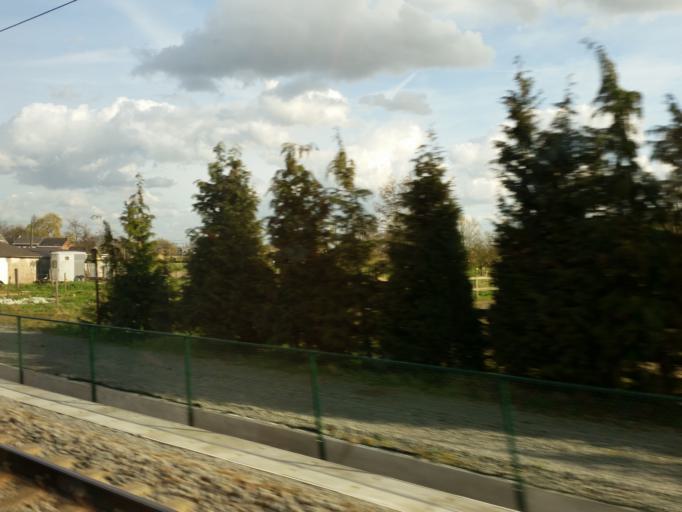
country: BE
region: Flanders
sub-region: Provincie Vlaams-Brabant
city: Kapelle-op-den-Bos
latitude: 51.0131
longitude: 4.4130
